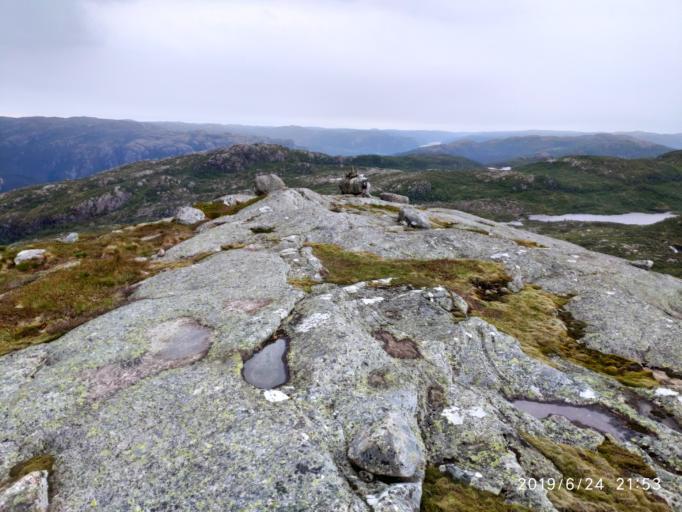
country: NO
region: Vest-Agder
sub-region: Sirdal
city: Tonstad
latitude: 58.7643
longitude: 6.7080
